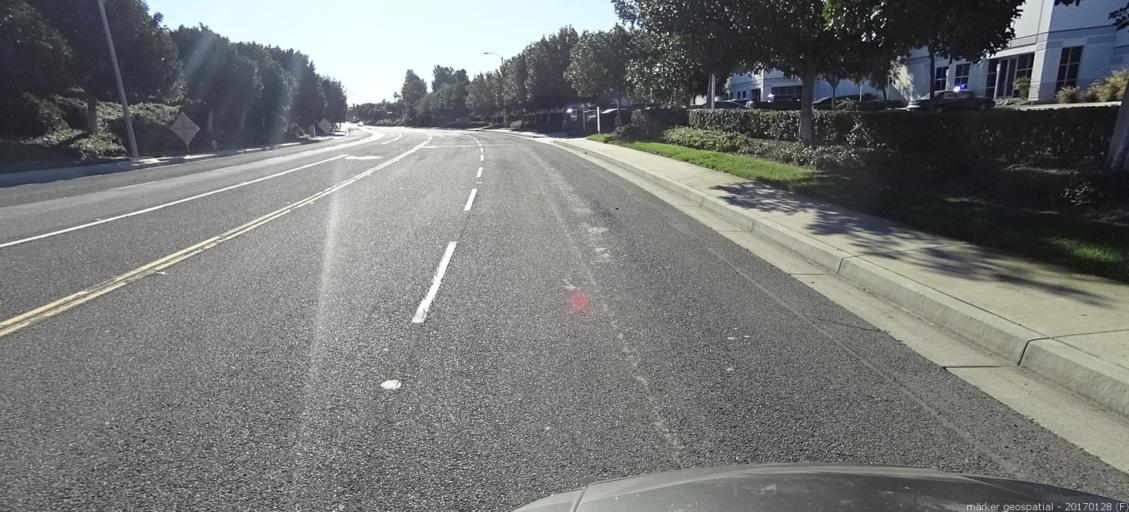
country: US
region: California
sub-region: Orange County
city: Lake Forest
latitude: 33.6672
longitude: -117.6884
